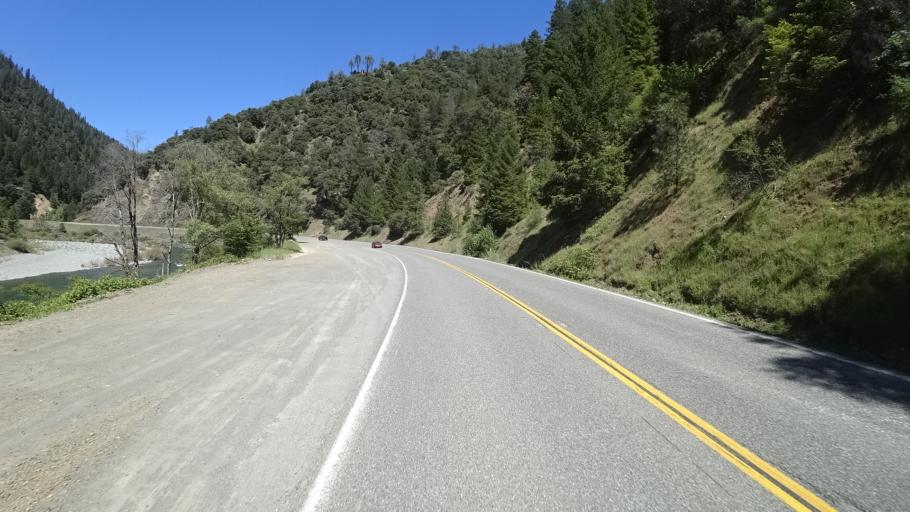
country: US
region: California
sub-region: Trinity County
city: Hayfork
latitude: 40.7768
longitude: -123.3075
